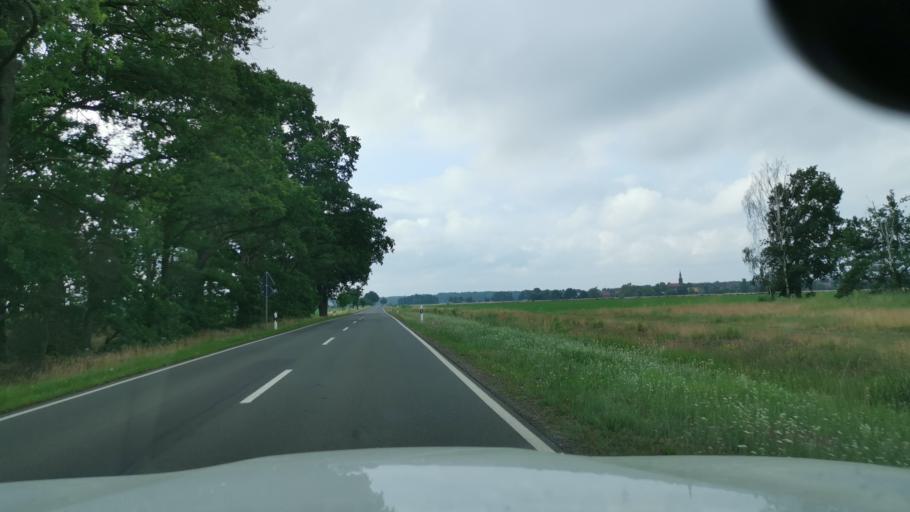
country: DE
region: Saxony-Anhalt
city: Annaburg
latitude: 51.7722
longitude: 13.0270
